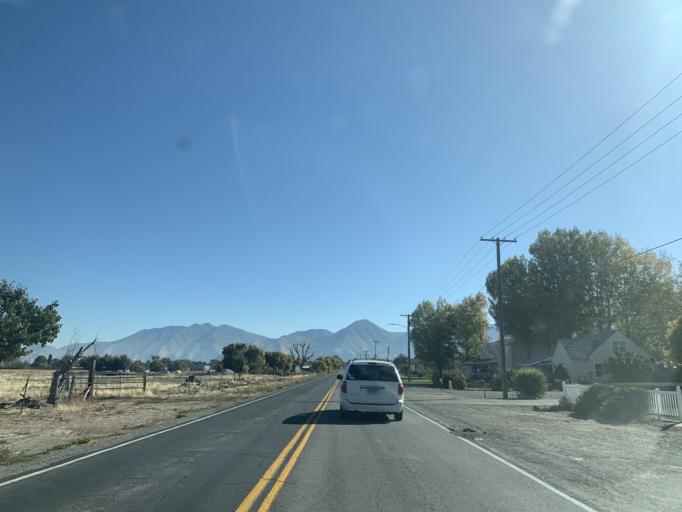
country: US
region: Utah
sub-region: Utah County
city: Payson
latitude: 40.0437
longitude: -111.7567
